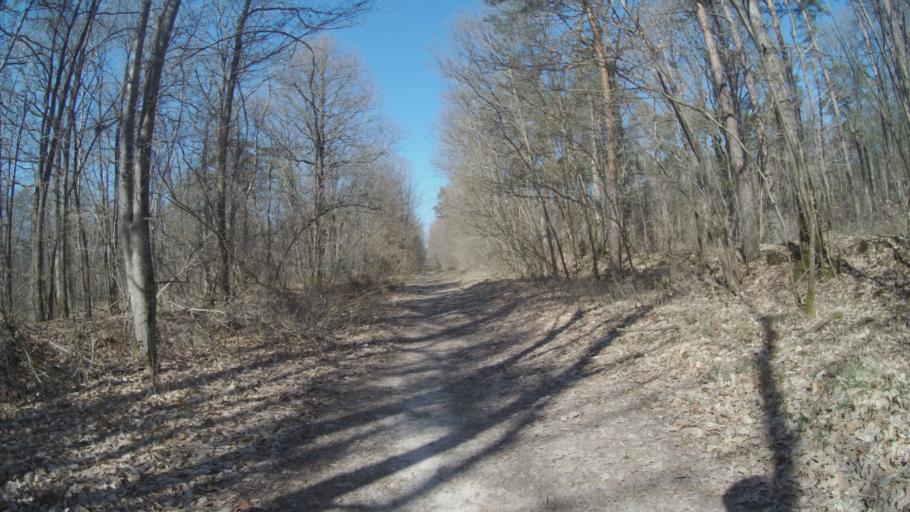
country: FR
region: Centre
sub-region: Departement du Loiret
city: Chanteau
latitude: 47.9475
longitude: 1.9820
